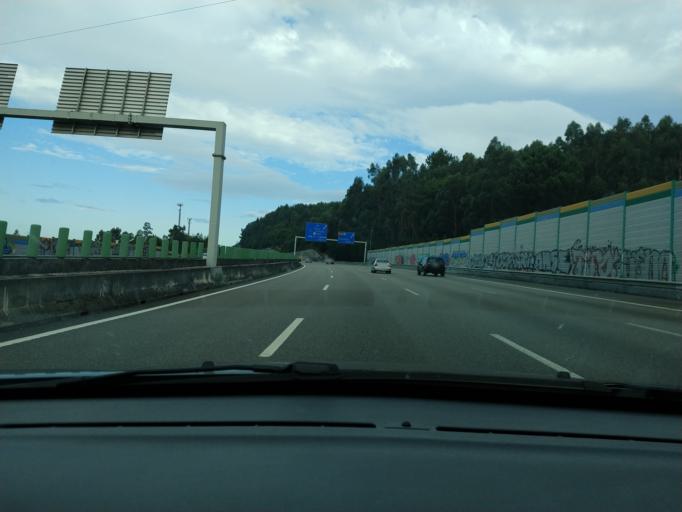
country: PT
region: Porto
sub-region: Vila Nova de Gaia
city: Perozinho
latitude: 41.0504
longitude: -8.5718
